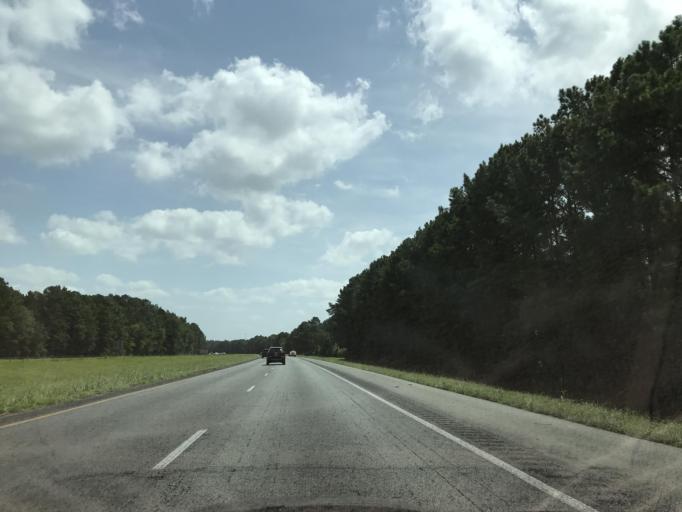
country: US
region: North Carolina
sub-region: Duplin County
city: Warsaw
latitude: 34.9807
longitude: -78.1297
